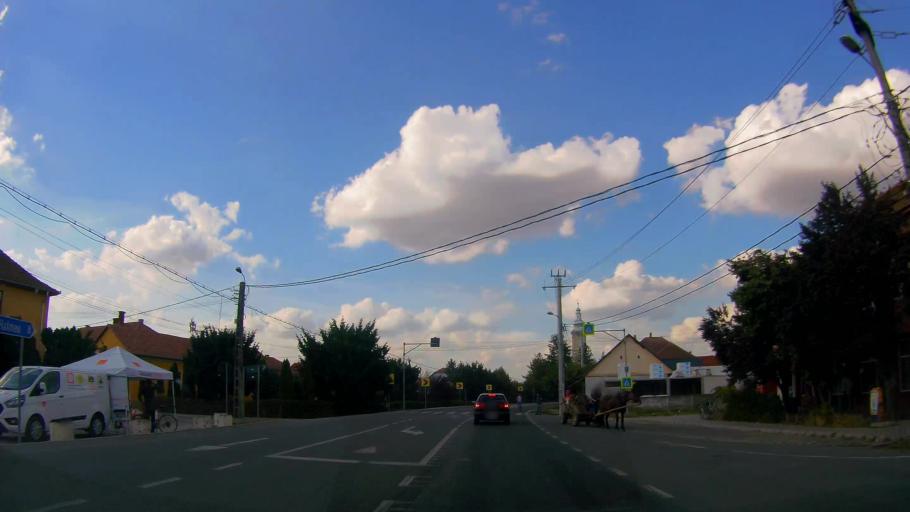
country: RO
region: Satu Mare
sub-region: Comuna Turulung
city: Turulung
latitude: 47.9327
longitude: 23.0832
